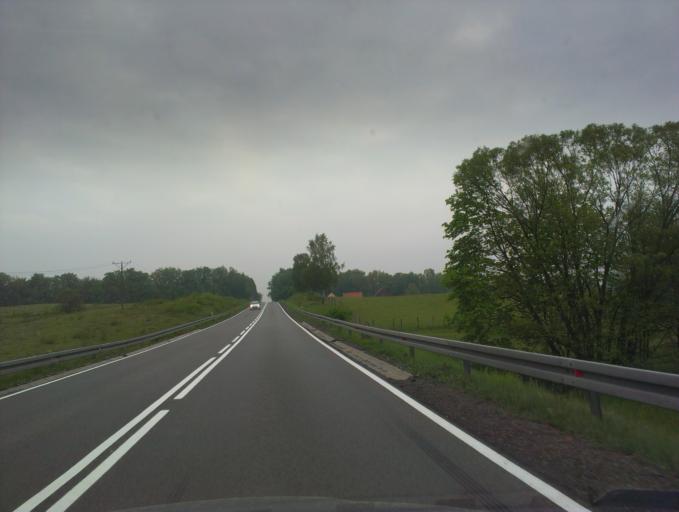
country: PL
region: West Pomeranian Voivodeship
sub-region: Powiat koszalinski
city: Bobolice
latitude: 53.8827
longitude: 16.6135
